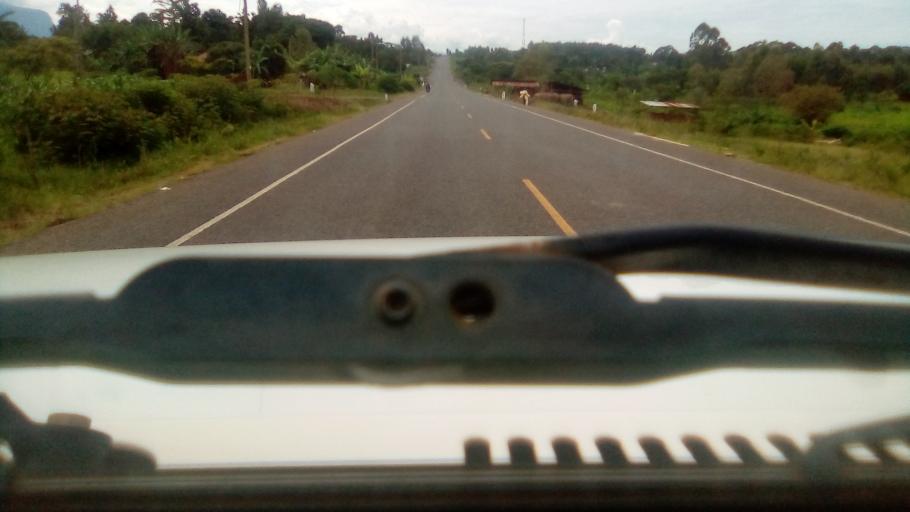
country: UG
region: Eastern Region
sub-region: Mbale District
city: Mbale
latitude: 0.9860
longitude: 34.1817
